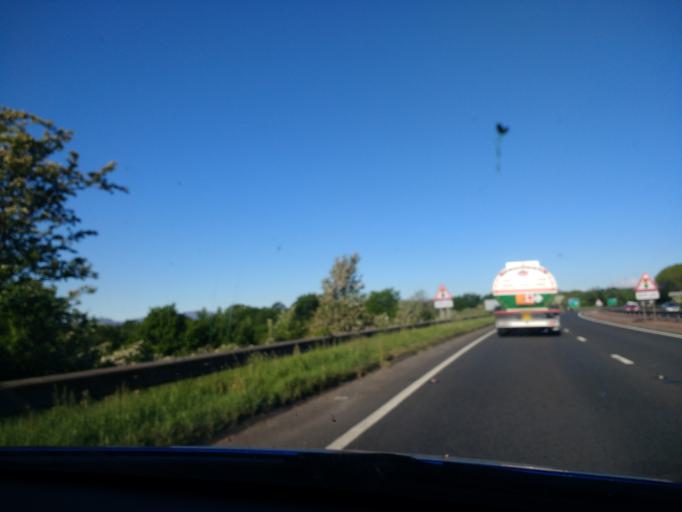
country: GB
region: England
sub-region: Cumbria
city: Penrith
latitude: 54.6521
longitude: -2.7576
